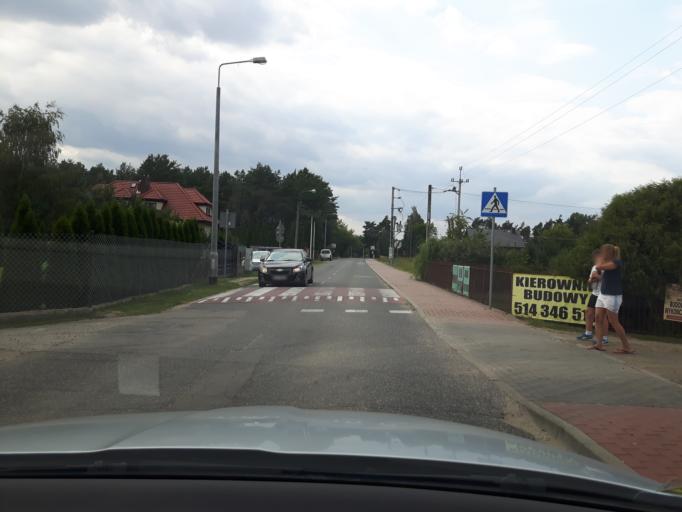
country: PL
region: Masovian Voivodeship
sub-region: Powiat legionowski
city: Wieliszew
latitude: 52.4704
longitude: 20.9290
